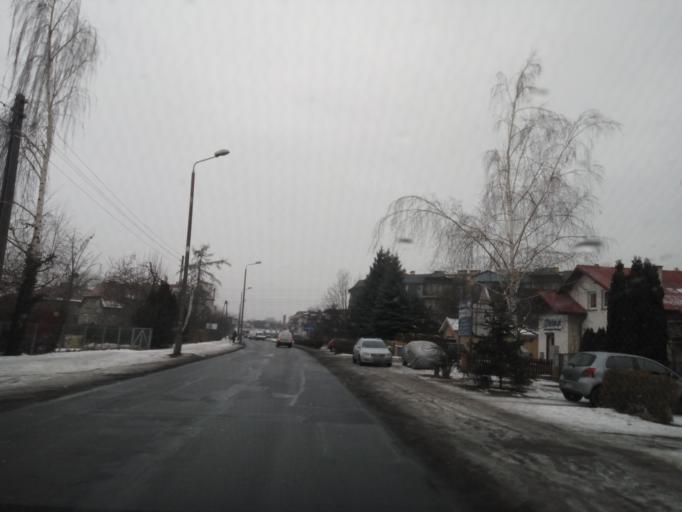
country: PL
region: Lower Silesian Voivodeship
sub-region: Powiat wroclawski
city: Wroclaw
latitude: 51.0612
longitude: 17.0281
